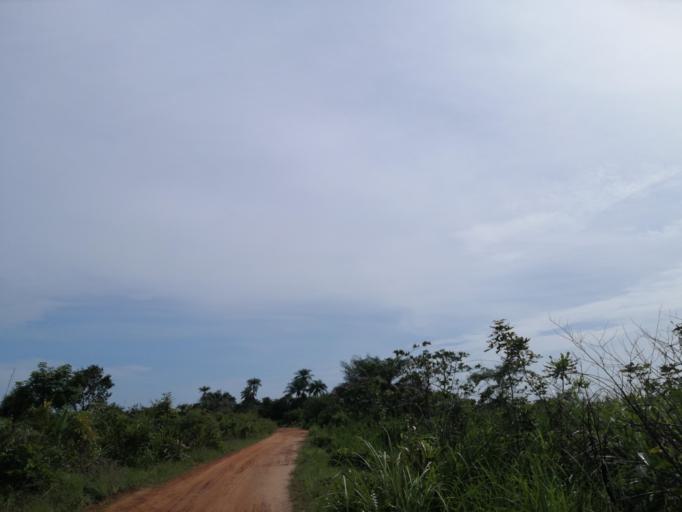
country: SL
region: Northern Province
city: Port Loko
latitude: 8.7939
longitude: -12.9237
